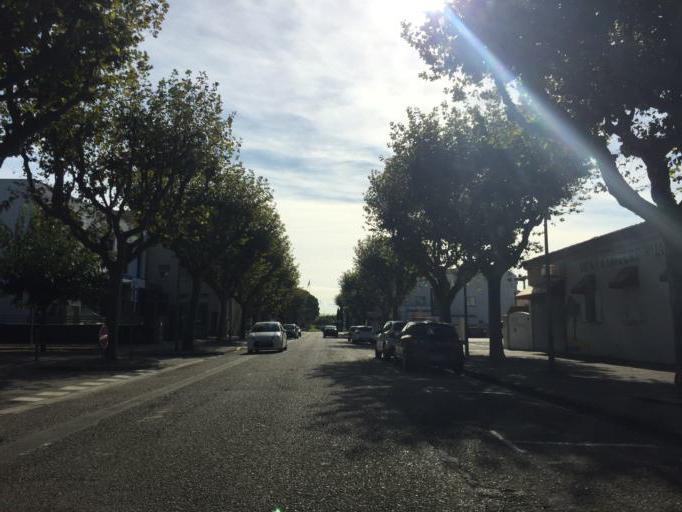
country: FR
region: Rhone-Alpes
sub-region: Departement de la Drome
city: Pierrelatte
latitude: 44.3777
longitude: 4.6996
